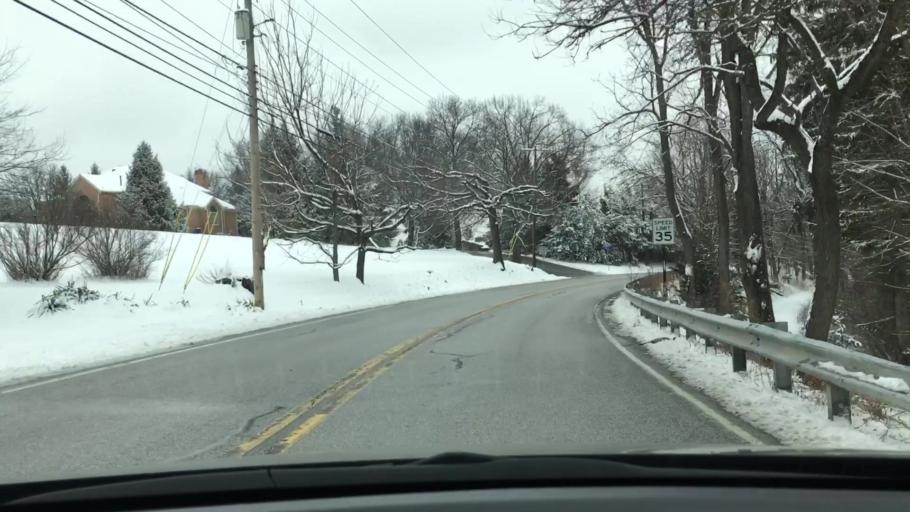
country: US
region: Pennsylvania
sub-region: York County
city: Grantley
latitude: 39.9336
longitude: -76.7263
